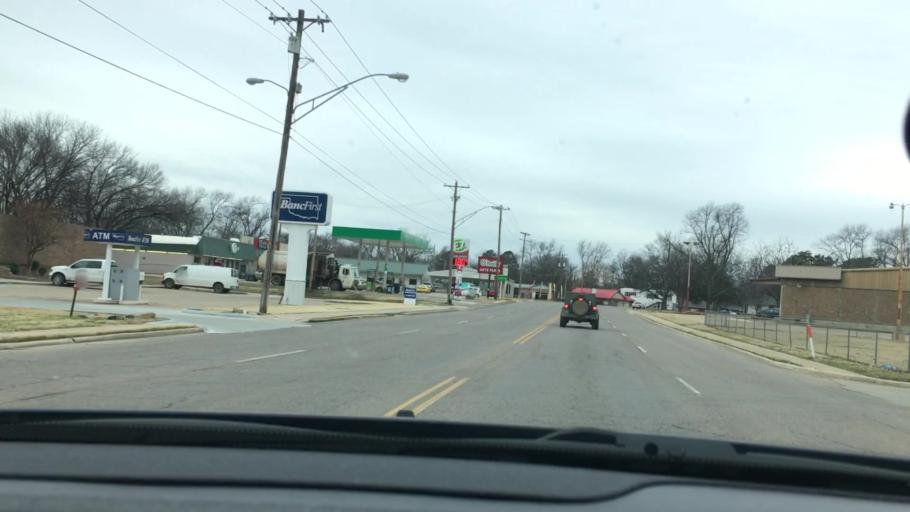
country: US
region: Oklahoma
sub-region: Johnston County
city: Tishomingo
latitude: 34.2306
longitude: -96.6681
